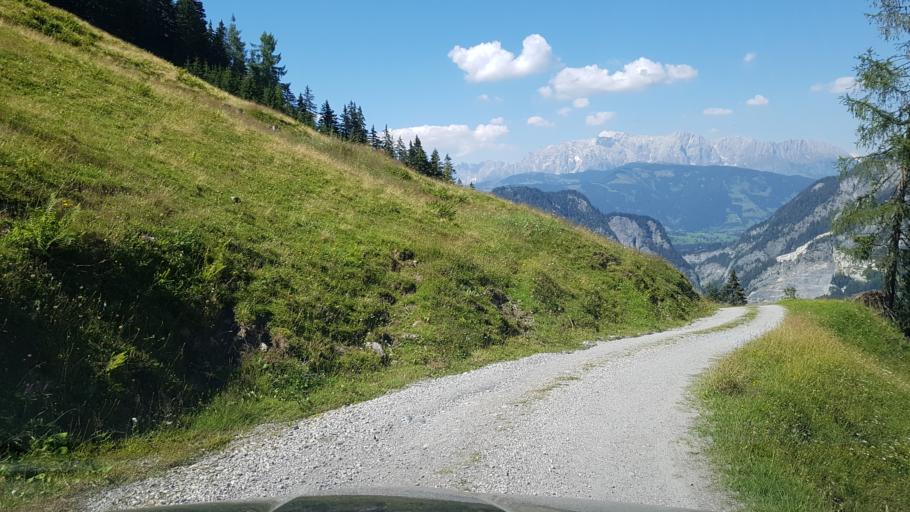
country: AT
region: Salzburg
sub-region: Politischer Bezirk Sankt Johann im Pongau
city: Dorfgastein
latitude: 47.2445
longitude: 13.0736
